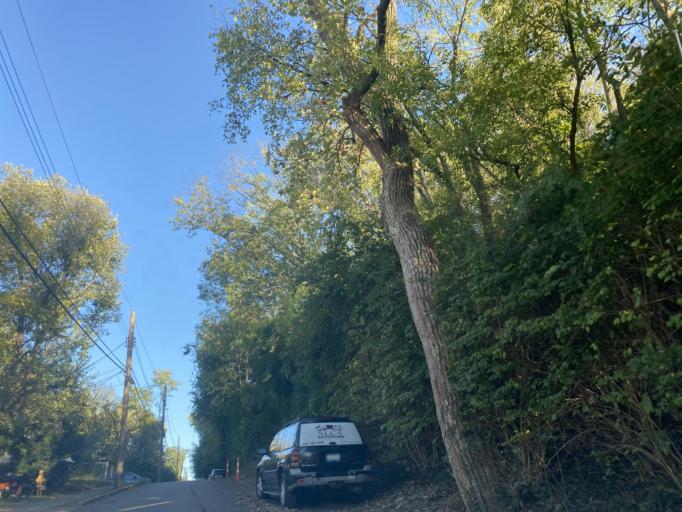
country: US
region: Kentucky
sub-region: Campbell County
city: Dayton
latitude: 39.1128
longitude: -84.4666
